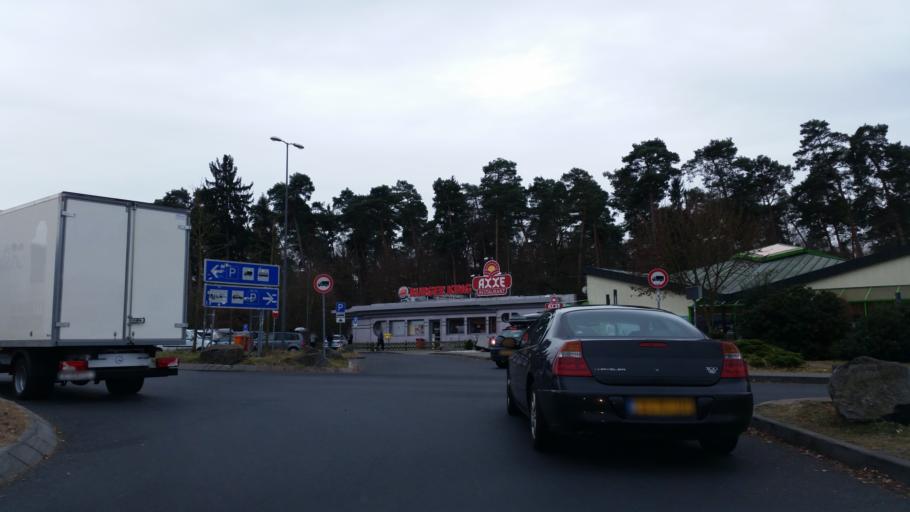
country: DE
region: Hesse
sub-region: Regierungsbezirk Darmstadt
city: Rodgau
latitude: 50.0552
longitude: 8.9071
